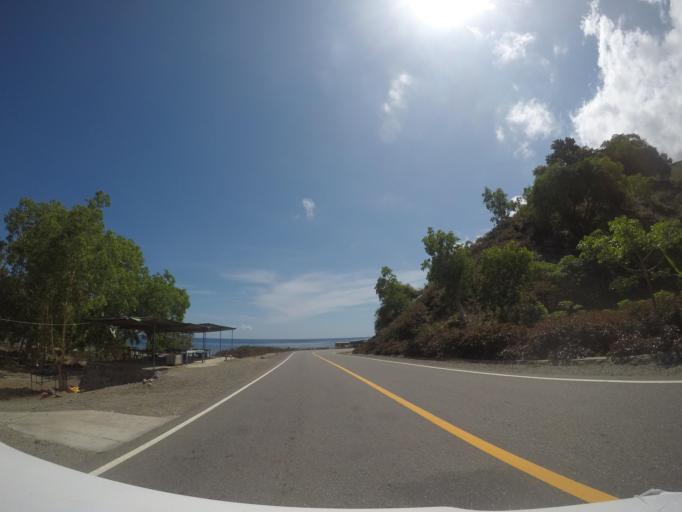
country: TL
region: Manatuto
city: Manatuto
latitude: -8.4768
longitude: 125.8837
